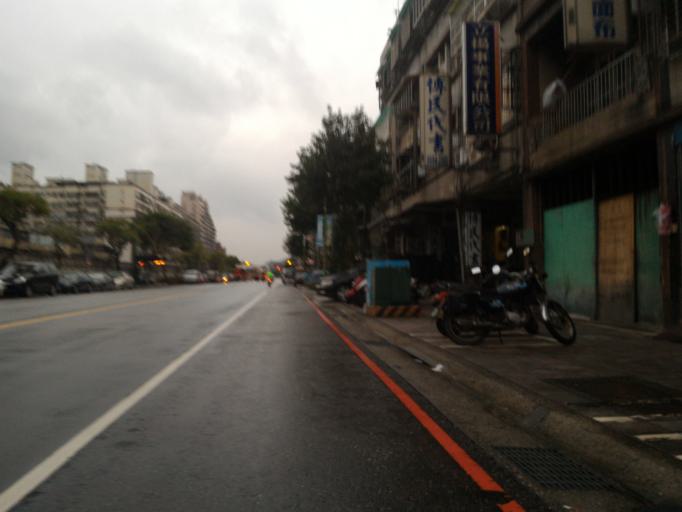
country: TW
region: Taipei
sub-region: Taipei
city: Banqiao
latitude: 24.9846
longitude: 121.4164
